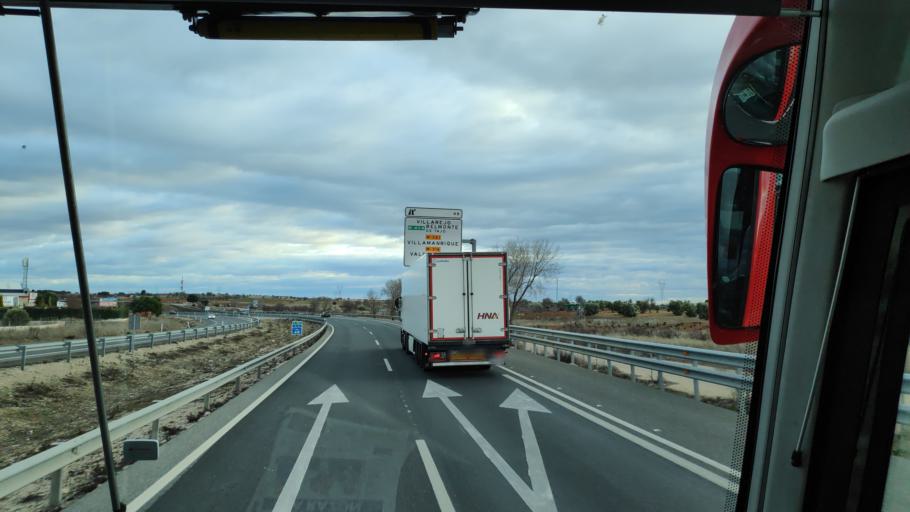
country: ES
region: Madrid
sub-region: Provincia de Madrid
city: Villarejo de Salvanes
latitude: 40.1759
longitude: -3.2957
